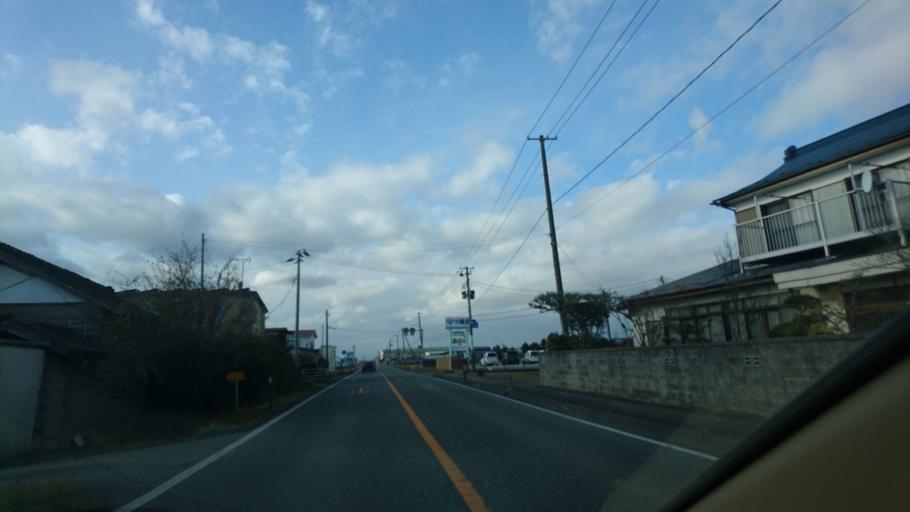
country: JP
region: Miyagi
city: Kogota
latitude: 38.5520
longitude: 141.0916
